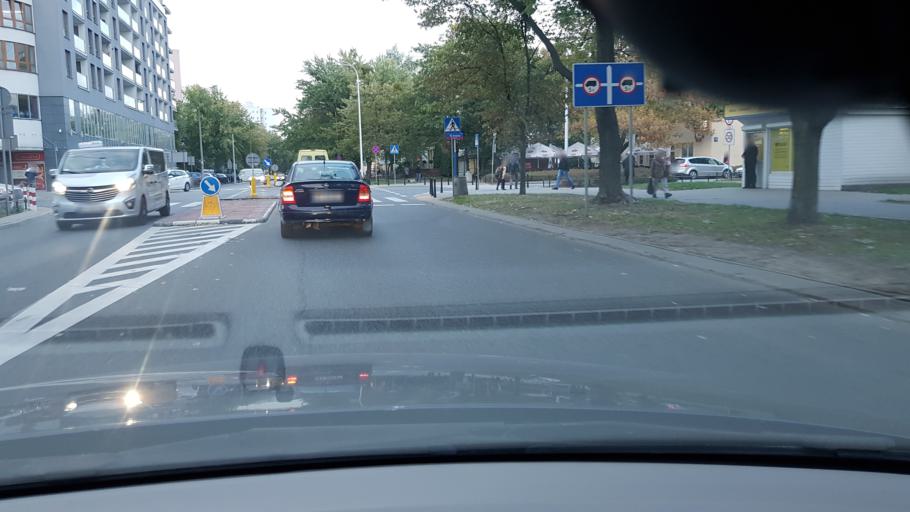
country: PL
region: Masovian Voivodeship
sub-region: Warszawa
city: Bielany
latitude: 52.2906
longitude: 20.9359
